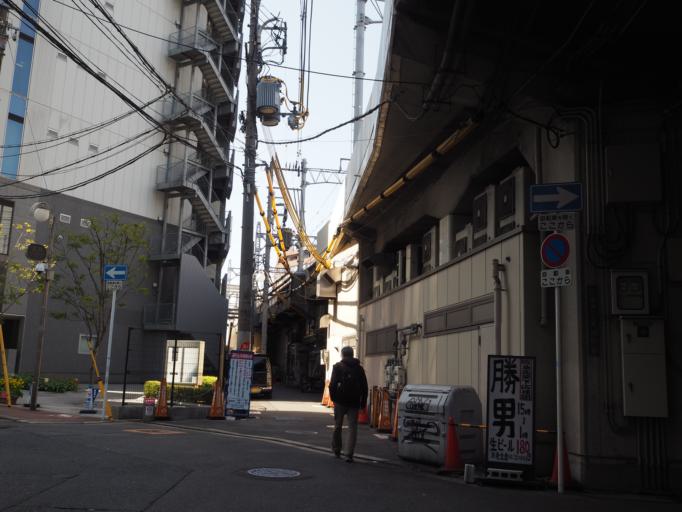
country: JP
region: Osaka
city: Osaka-shi
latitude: 34.7078
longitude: 135.4974
